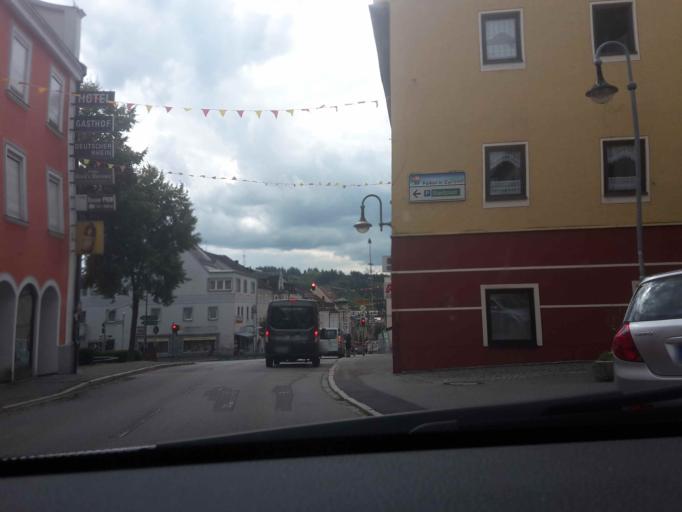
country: DE
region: Bavaria
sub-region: Lower Bavaria
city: Zwiesel
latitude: 49.0142
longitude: 13.2329
